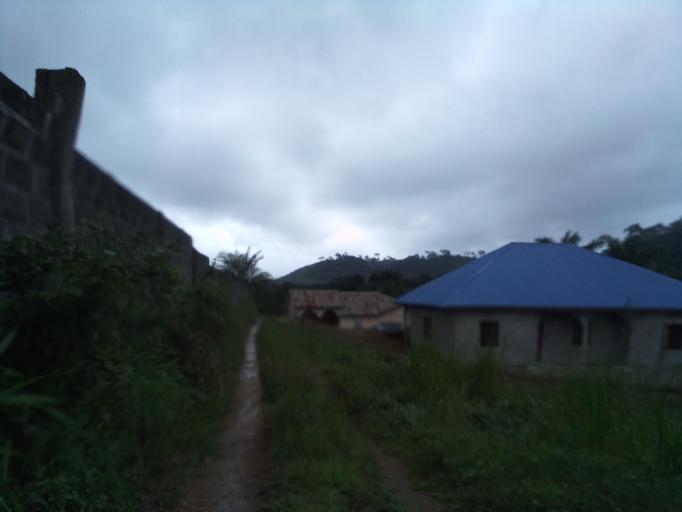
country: SL
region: Eastern Province
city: Kenema
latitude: 7.8554
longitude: -11.2103
